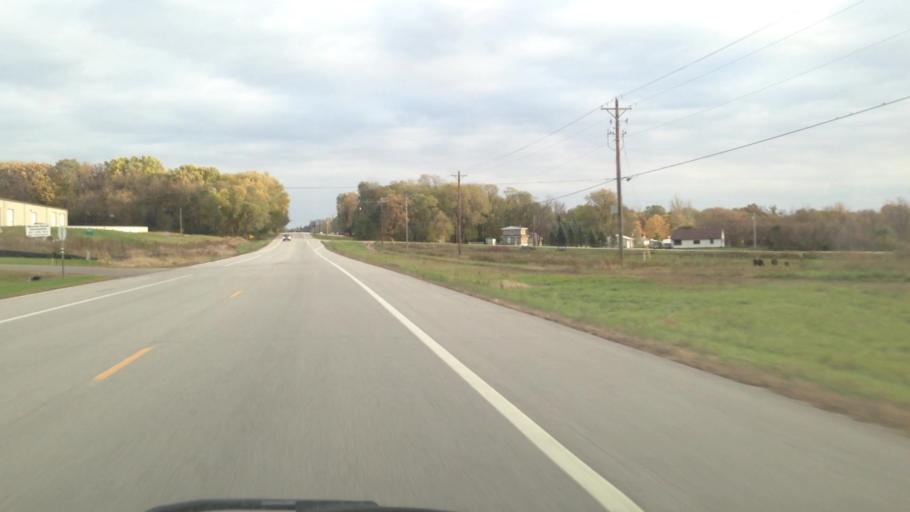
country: US
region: Minnesota
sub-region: Olmsted County
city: Rochester
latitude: 43.9803
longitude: -92.3989
